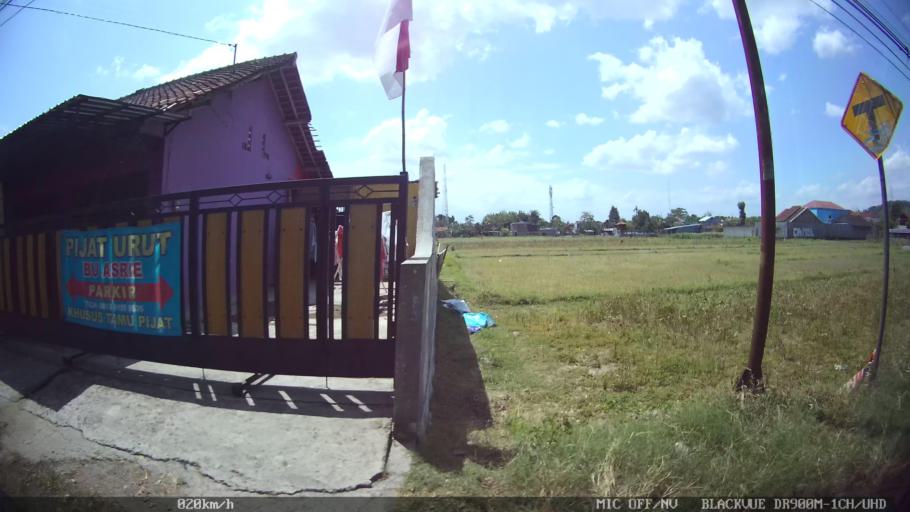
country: ID
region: Daerah Istimewa Yogyakarta
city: Sewon
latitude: -7.8984
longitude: 110.3828
